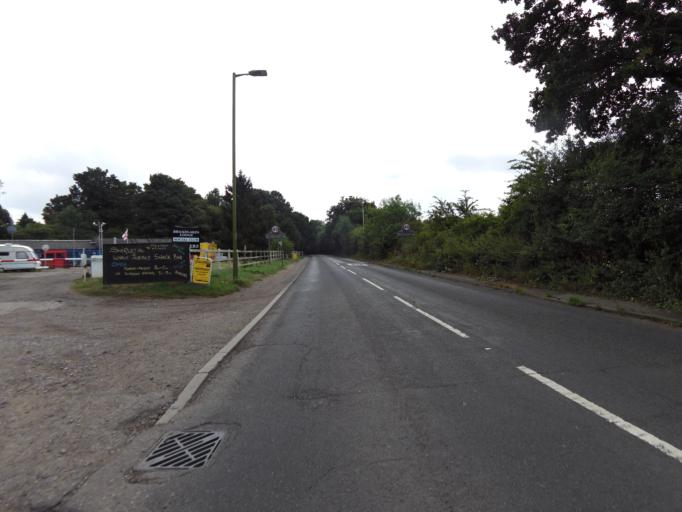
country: GB
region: England
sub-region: Hertfordshire
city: Shenley AV
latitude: 51.7165
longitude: -0.2998
